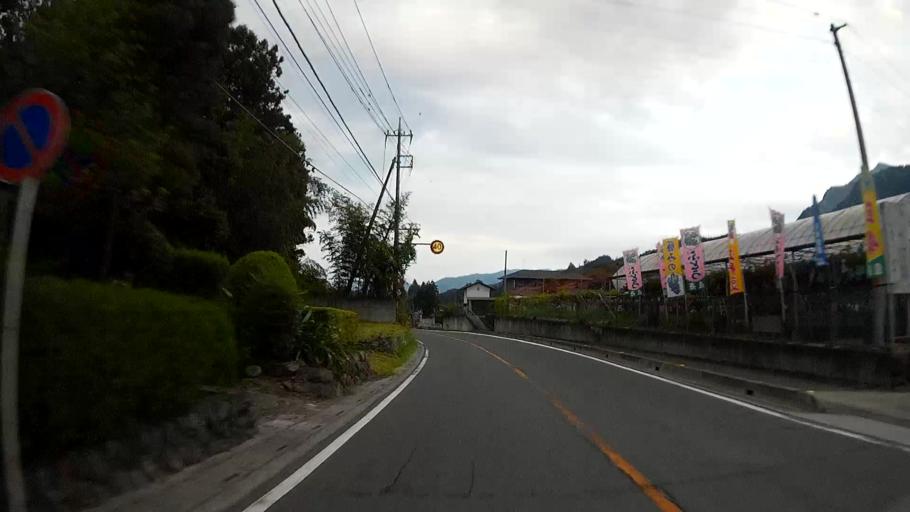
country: JP
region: Saitama
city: Chichibu
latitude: 35.9636
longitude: 139.0534
